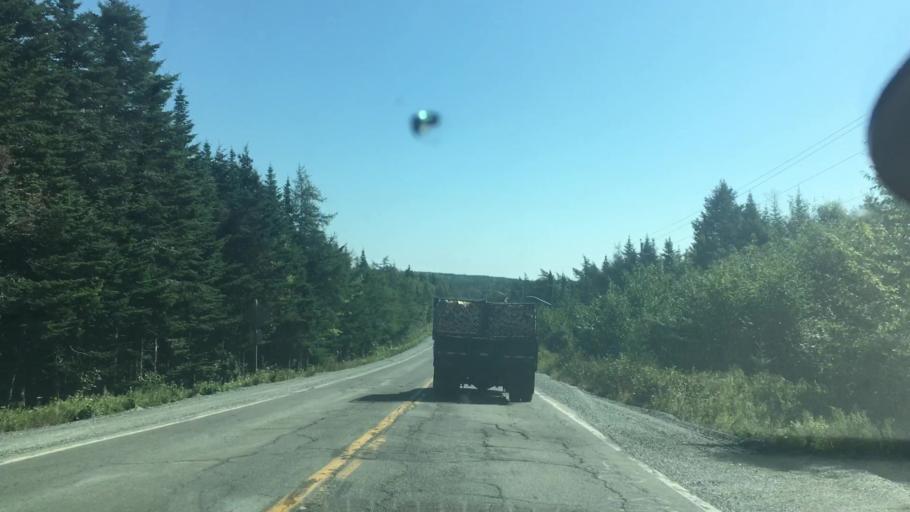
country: CA
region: Nova Scotia
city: New Glasgow
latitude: 44.9044
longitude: -62.4658
